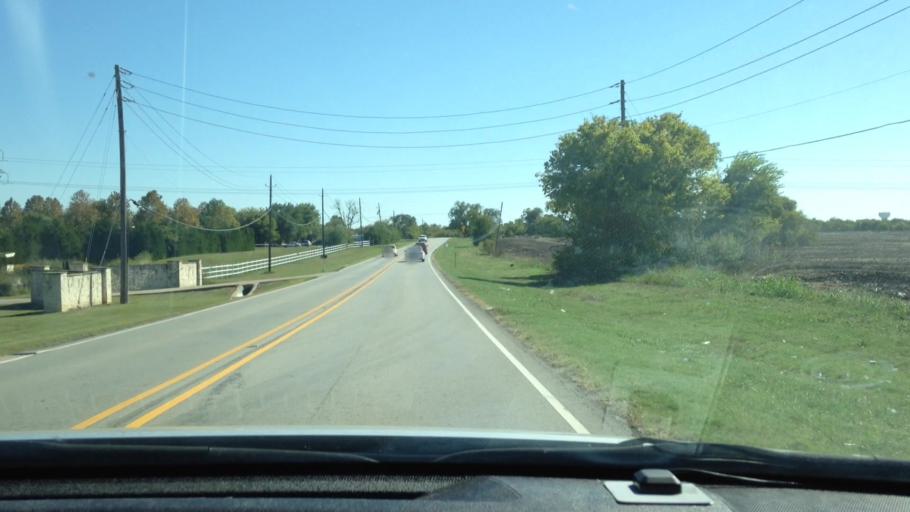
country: US
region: Texas
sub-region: Collin County
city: Lucas
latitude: 33.0654
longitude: -96.5701
